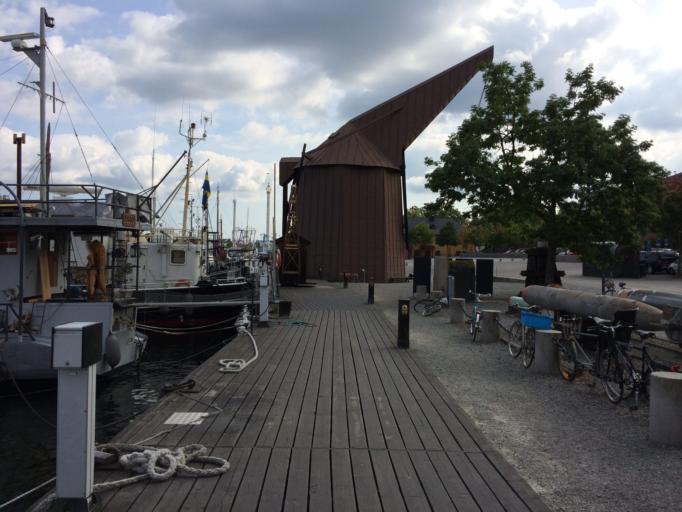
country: SE
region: Stockholm
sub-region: Stockholms Kommun
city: OEstermalm
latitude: 59.3276
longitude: 18.0840
